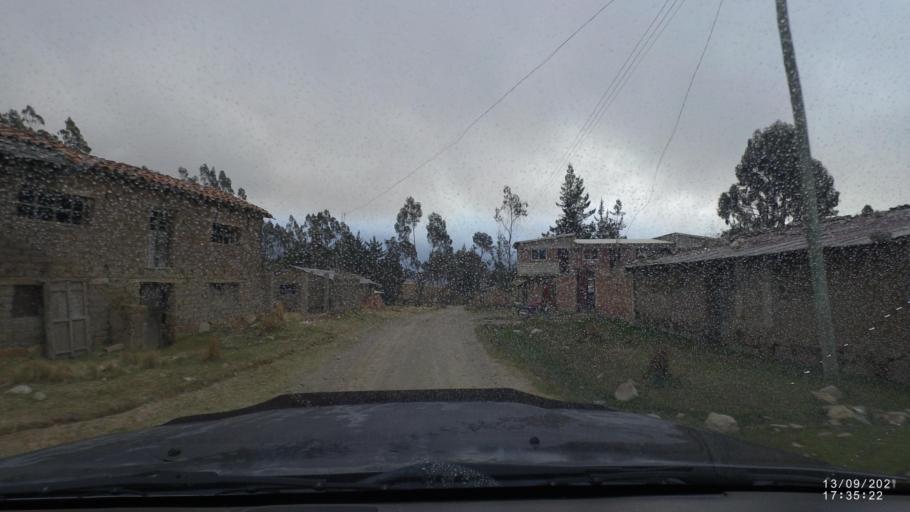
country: BO
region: Cochabamba
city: Colomi
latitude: -17.3674
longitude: -65.7961
